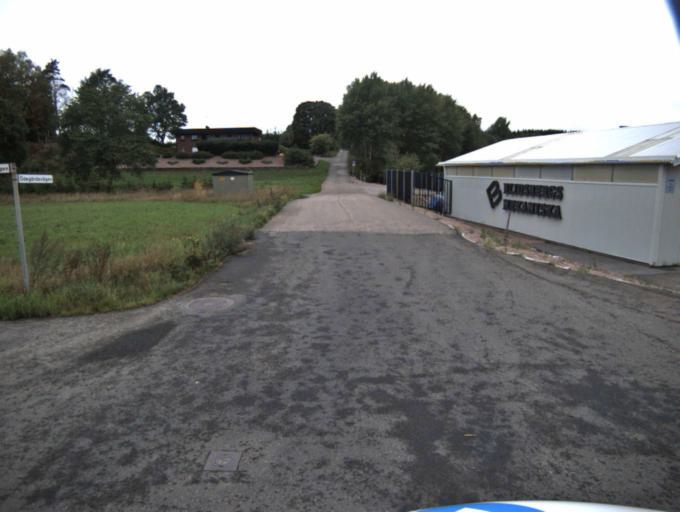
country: SE
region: Vaestra Goetaland
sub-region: Ulricehamns Kommun
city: Ulricehamn
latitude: 57.9212
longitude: 13.4893
